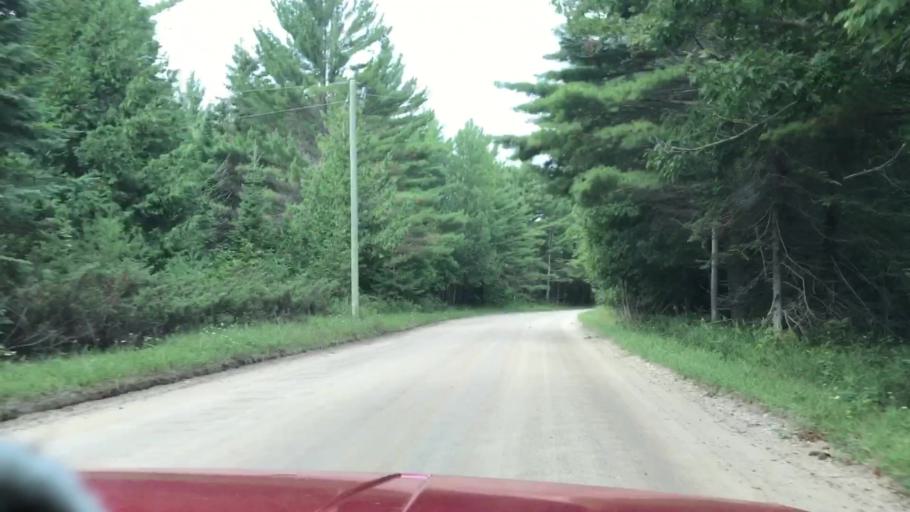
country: US
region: Michigan
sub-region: Charlevoix County
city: Charlevoix
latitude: 45.7278
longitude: -85.5353
